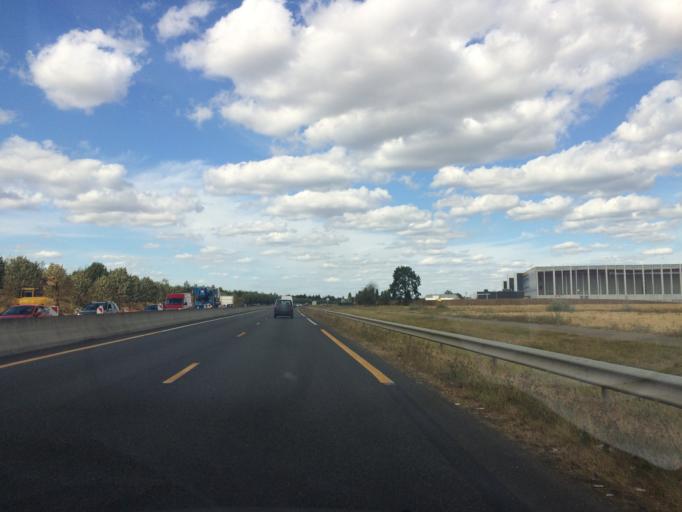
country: FR
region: Ile-de-France
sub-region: Departement de l'Essonne
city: Bretigny-sur-Orge
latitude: 48.5955
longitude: 2.3121
